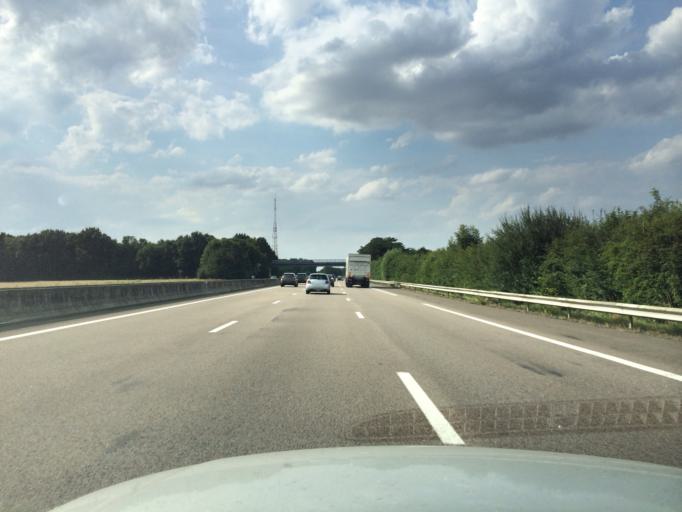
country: FR
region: Haute-Normandie
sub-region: Departement de l'Eure
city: La Chapelle-Reanville
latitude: 49.1002
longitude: 1.3529
